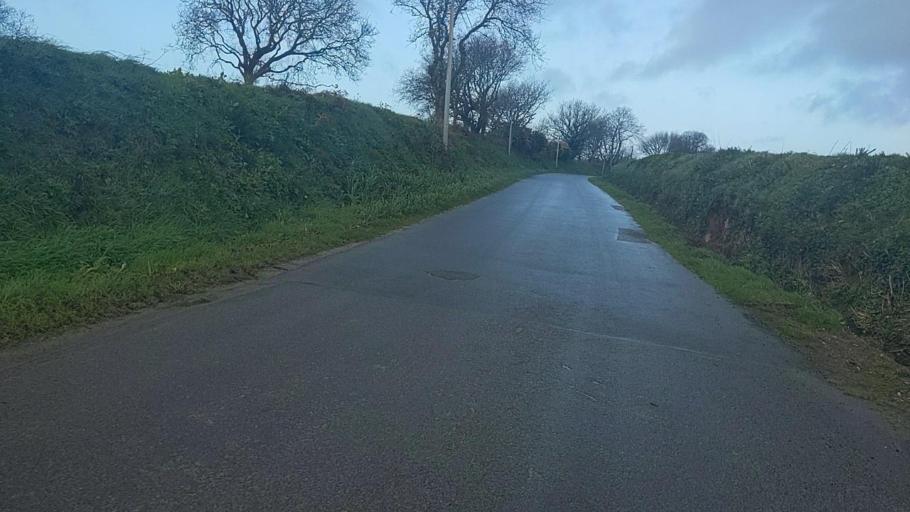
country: FR
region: Brittany
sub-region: Departement des Cotes-d'Armor
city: Pleumeur-Gautier
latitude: 48.8324
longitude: -3.1827
